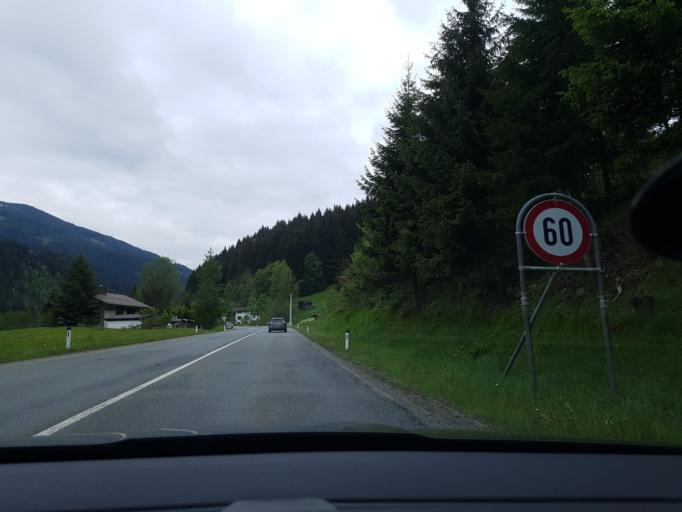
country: AT
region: Tyrol
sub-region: Politischer Bezirk Kitzbuhel
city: Jochberg
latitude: 47.3580
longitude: 12.4138
